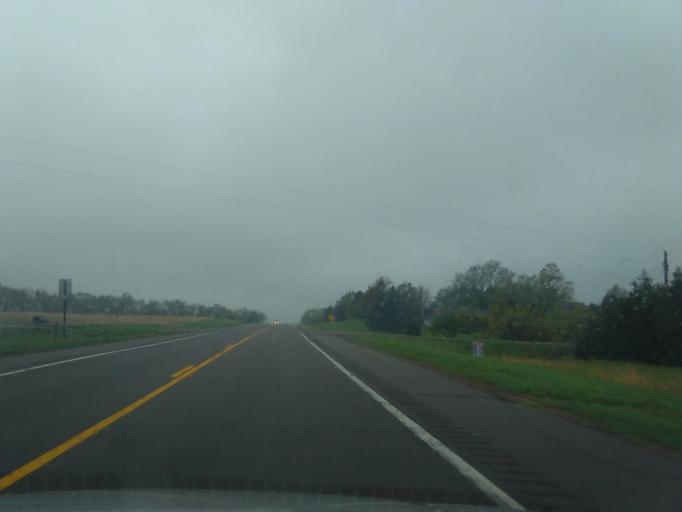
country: US
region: Nebraska
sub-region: Madison County
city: Norfolk
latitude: 42.0767
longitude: -97.3292
